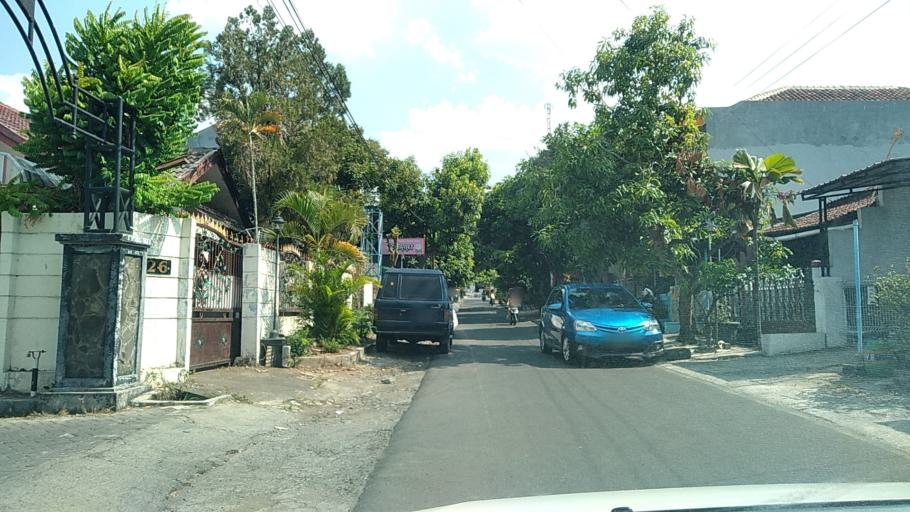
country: ID
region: Central Java
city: Ungaran
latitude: -7.0705
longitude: 110.4168
